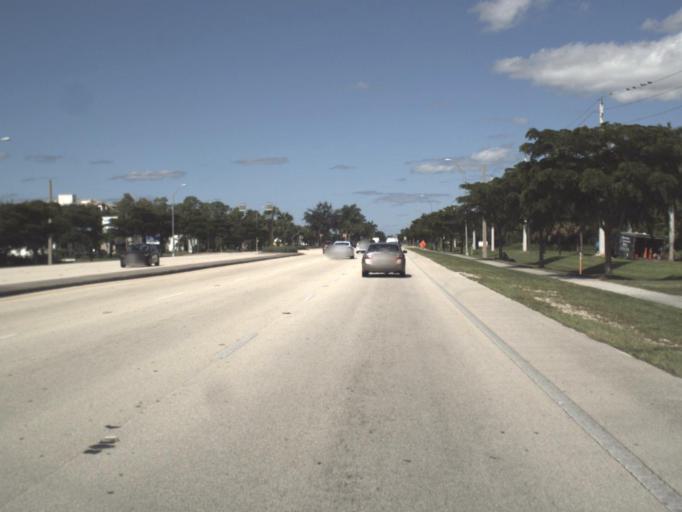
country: US
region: Florida
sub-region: Collier County
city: Lely
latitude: 26.1100
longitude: -81.7503
